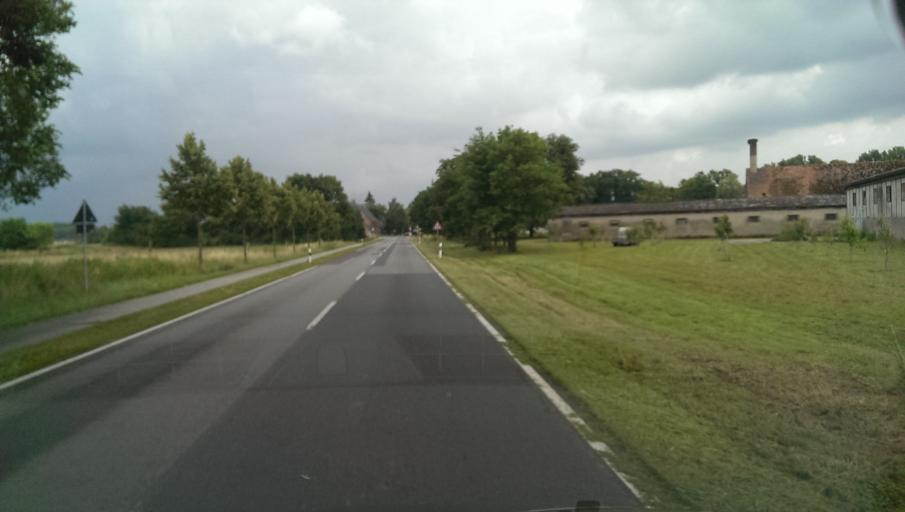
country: DE
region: Brandenburg
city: Rathenow
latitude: 52.6560
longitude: 12.3372
